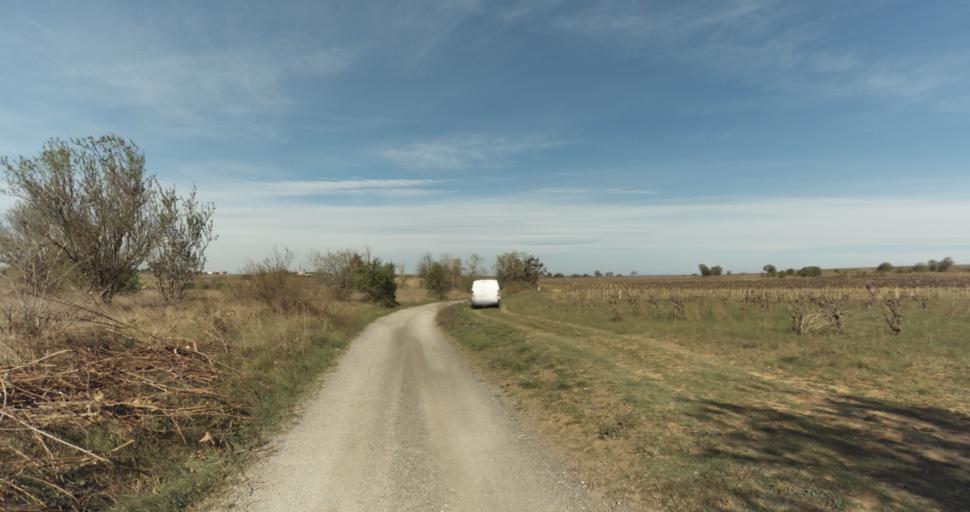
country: FR
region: Languedoc-Roussillon
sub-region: Departement de l'Herault
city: Marseillan
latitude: 43.3503
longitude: 3.4983
